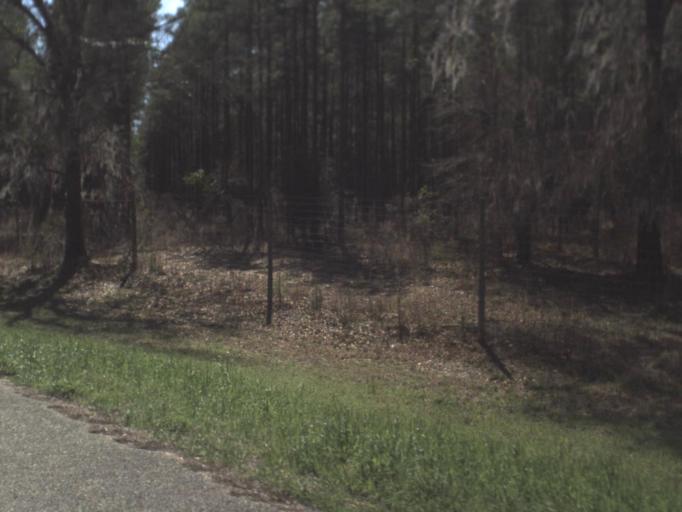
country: US
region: Florida
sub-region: Calhoun County
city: Blountstown
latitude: 30.5931
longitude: -85.0265
